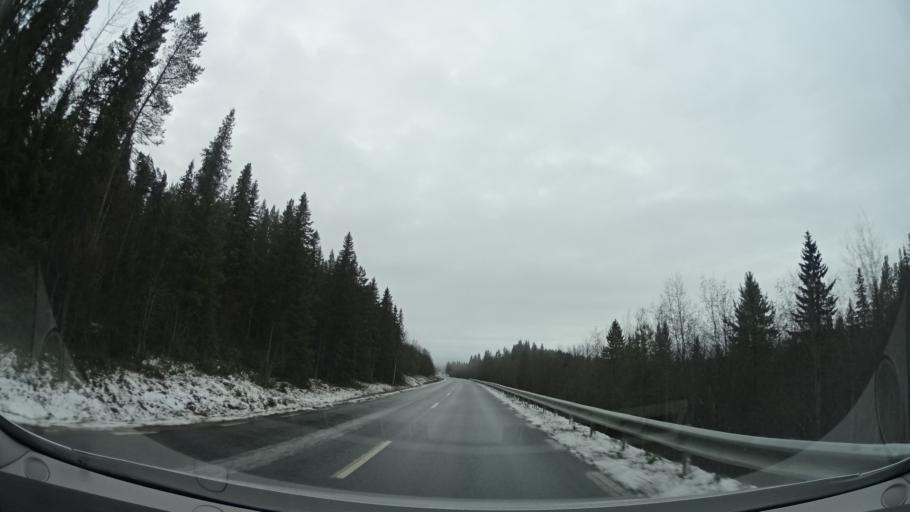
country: SE
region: Jaemtland
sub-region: Stroemsunds Kommun
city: Stroemsund
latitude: 64.0080
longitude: 15.5171
